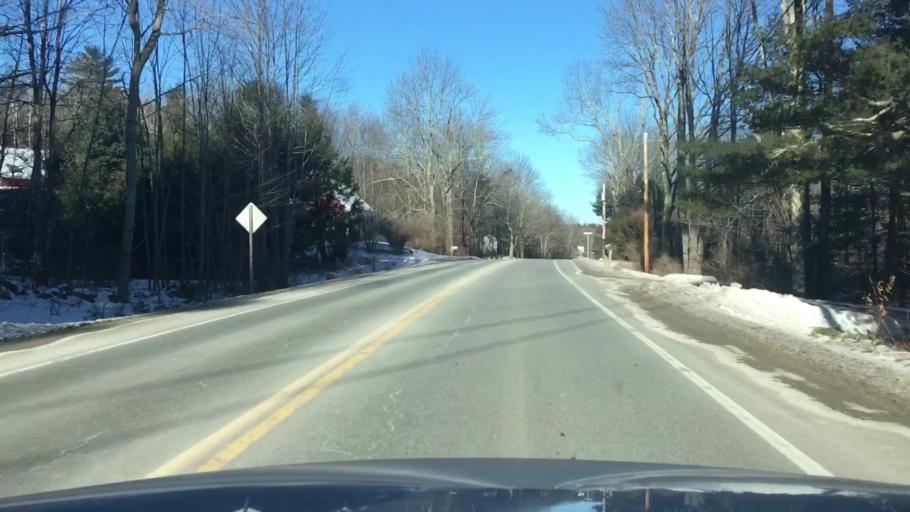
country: US
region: Maine
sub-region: Cumberland County
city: Freeport
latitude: 43.8788
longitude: -70.1093
